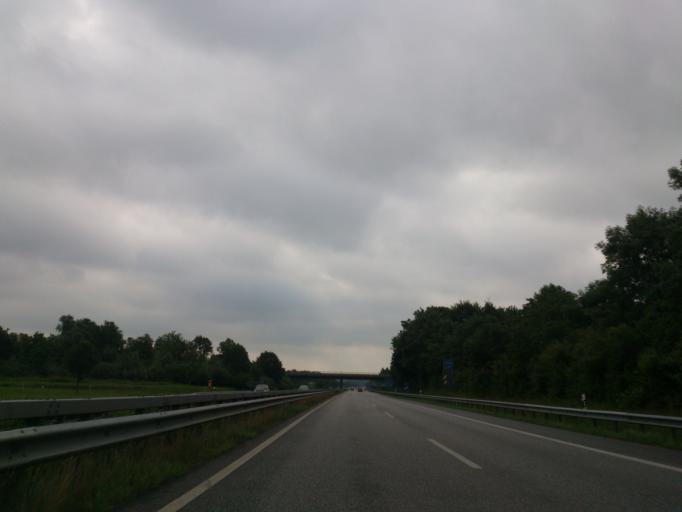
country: DE
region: Schleswig-Holstein
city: Agethorst
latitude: 54.0314
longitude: 9.4398
